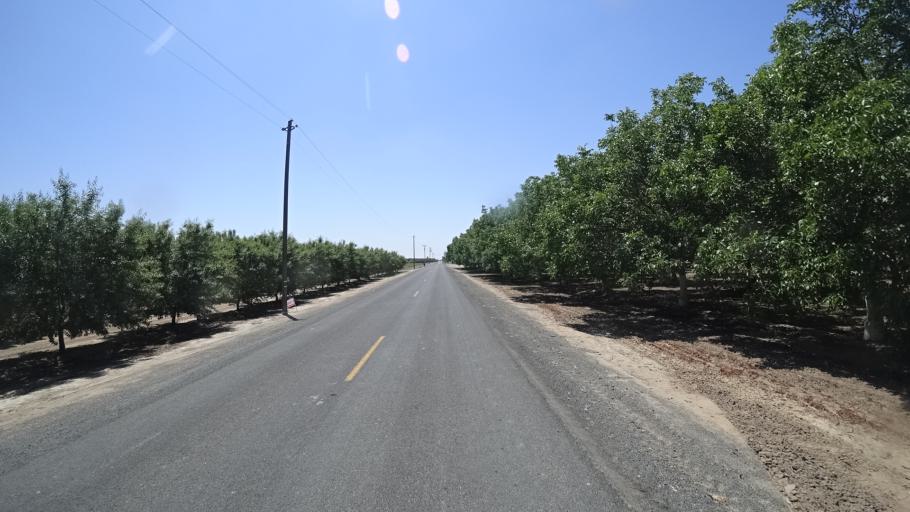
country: US
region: California
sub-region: Kings County
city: Armona
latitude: 36.2884
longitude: -119.7271
